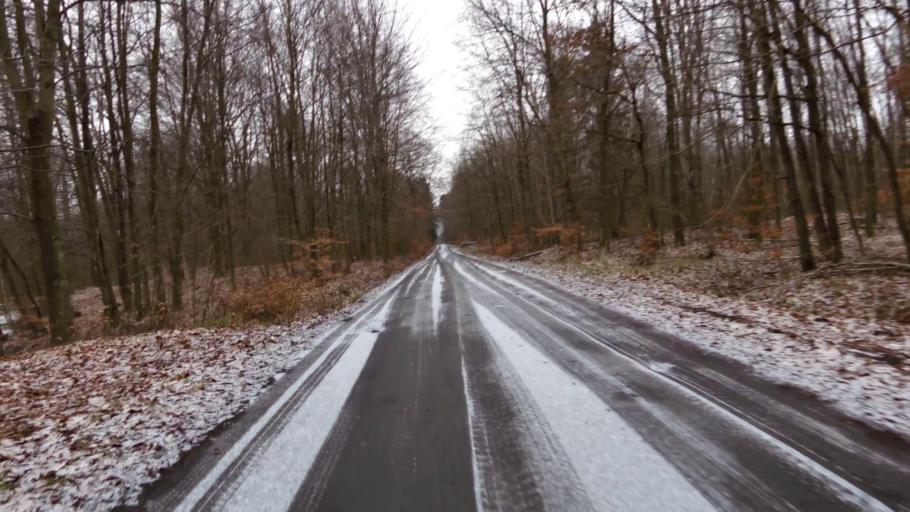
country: PL
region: West Pomeranian Voivodeship
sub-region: Powiat szczecinecki
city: Szczecinek
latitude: 53.6742
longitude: 16.6565
